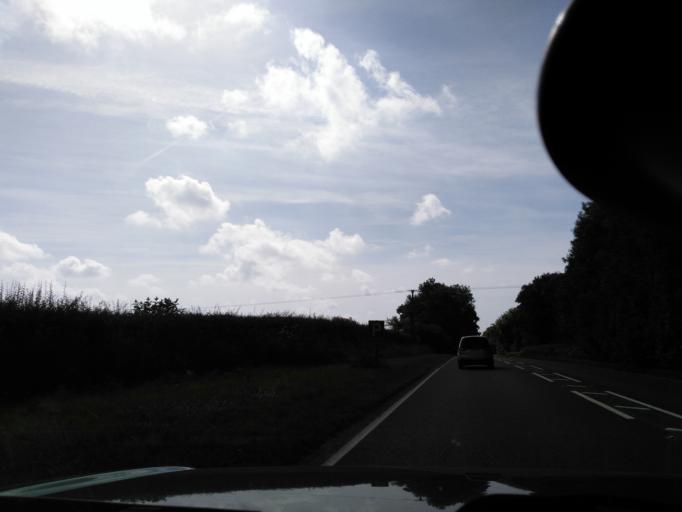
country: GB
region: England
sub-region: Wiltshire
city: Whiteparish
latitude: 51.0107
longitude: -1.6780
